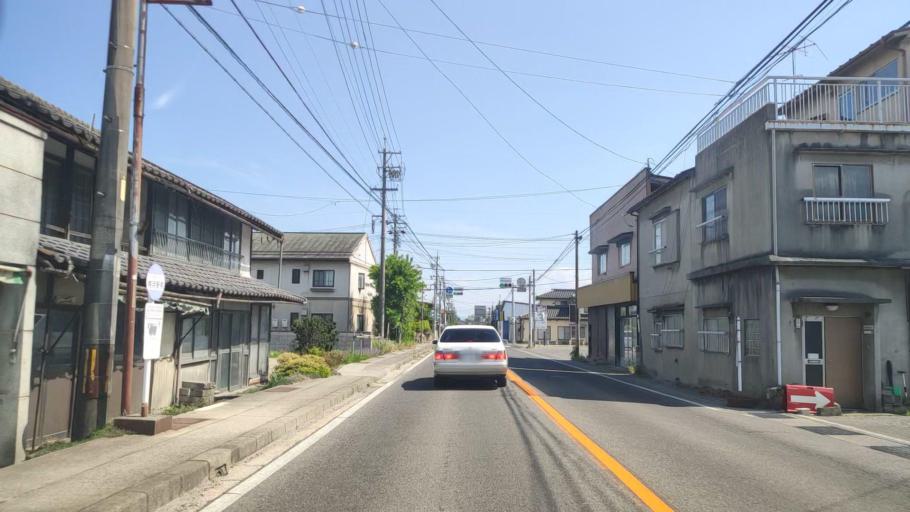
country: JP
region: Nagano
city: Hotaka
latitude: 36.3594
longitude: 137.8791
